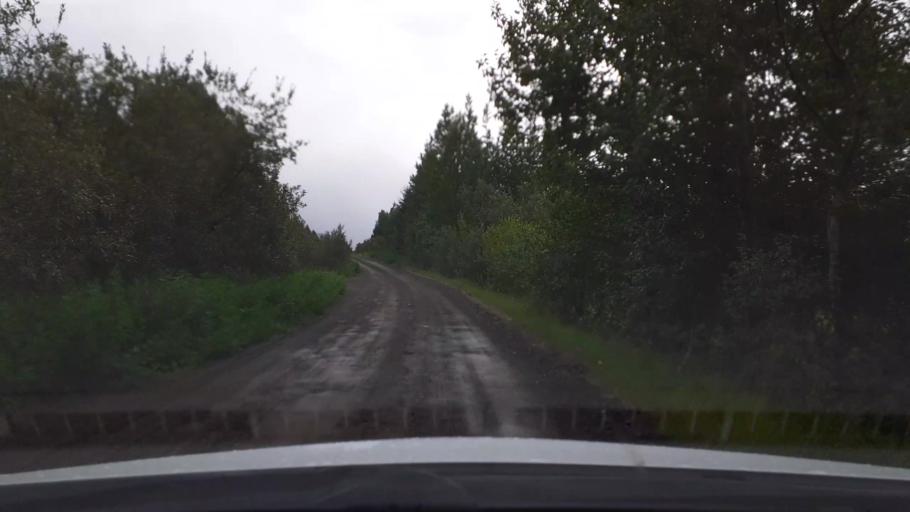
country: IS
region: Capital Region
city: Mosfellsbaer
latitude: 64.4956
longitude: -21.3539
